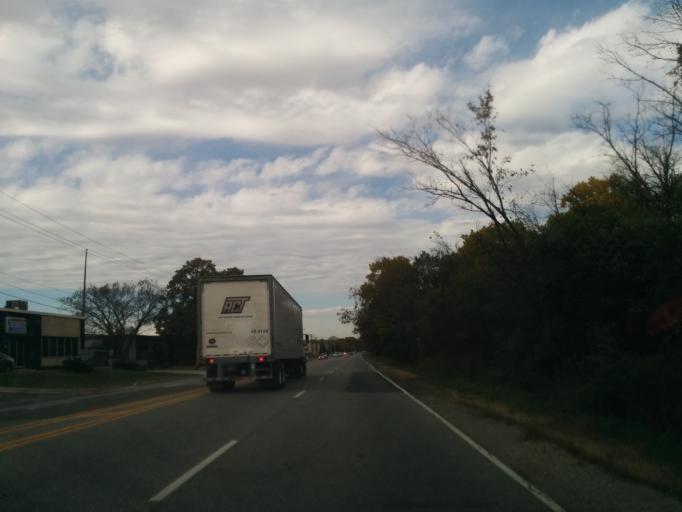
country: US
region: Illinois
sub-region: Cook County
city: Franklin Park
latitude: 41.9480
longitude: -87.8558
